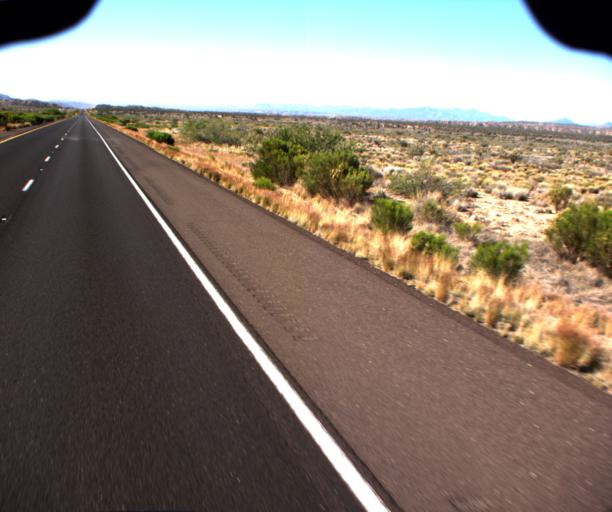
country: US
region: Arizona
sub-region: Mohave County
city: Kingman
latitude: 35.1084
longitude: -113.6667
